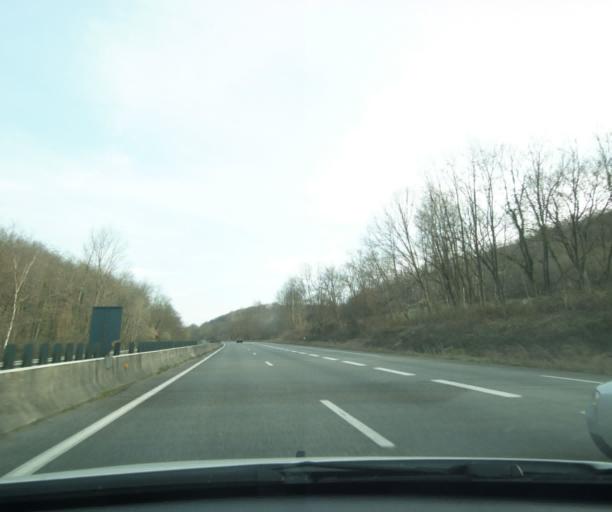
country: FR
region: Midi-Pyrenees
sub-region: Departement des Hautes-Pyrenees
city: Capvern
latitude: 43.1523
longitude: 0.2933
